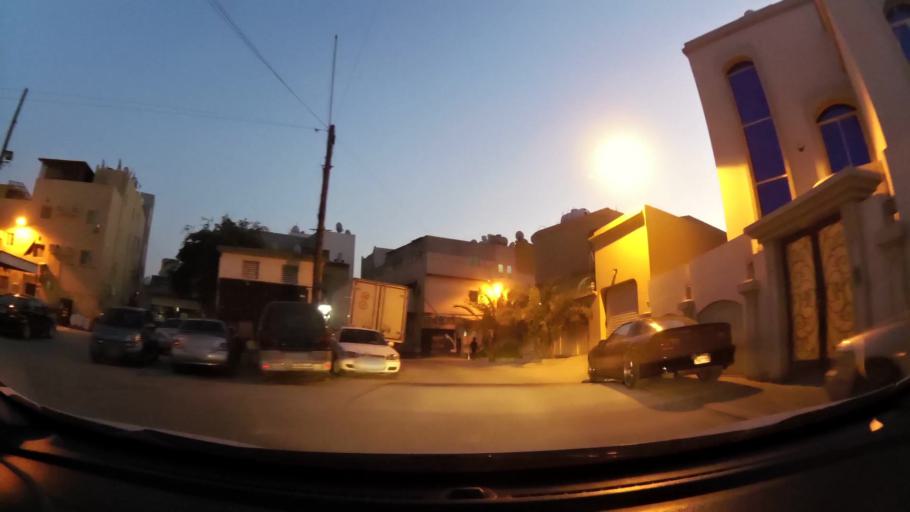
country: BH
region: Manama
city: Jidd Hafs
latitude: 26.2036
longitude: 50.5530
